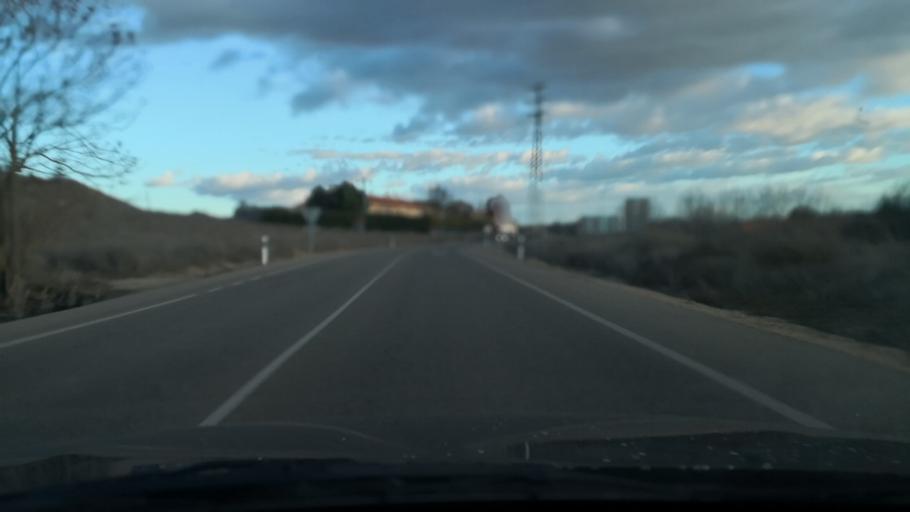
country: ES
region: Castille and Leon
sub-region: Provincia de Valladolid
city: Medina del Campo
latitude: 41.3137
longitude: -4.9068
